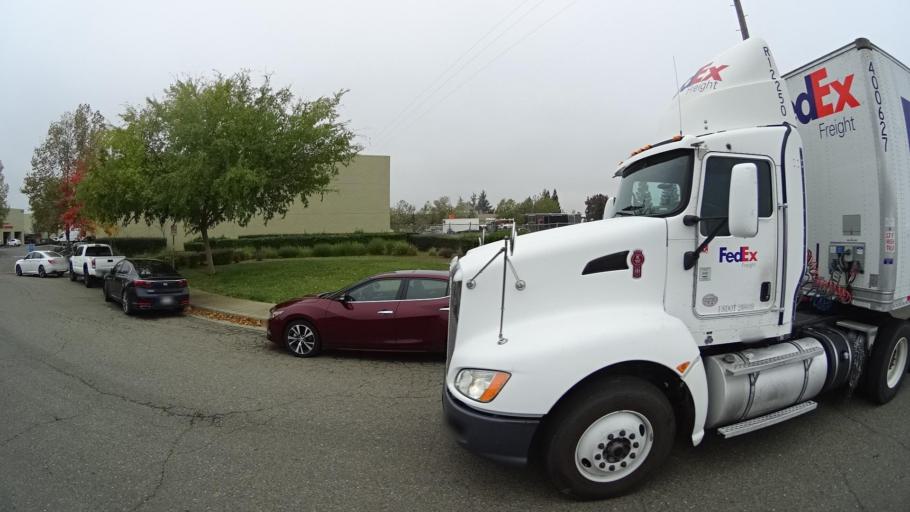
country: US
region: California
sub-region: Sacramento County
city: Elk Grove
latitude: 38.3845
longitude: -121.3584
